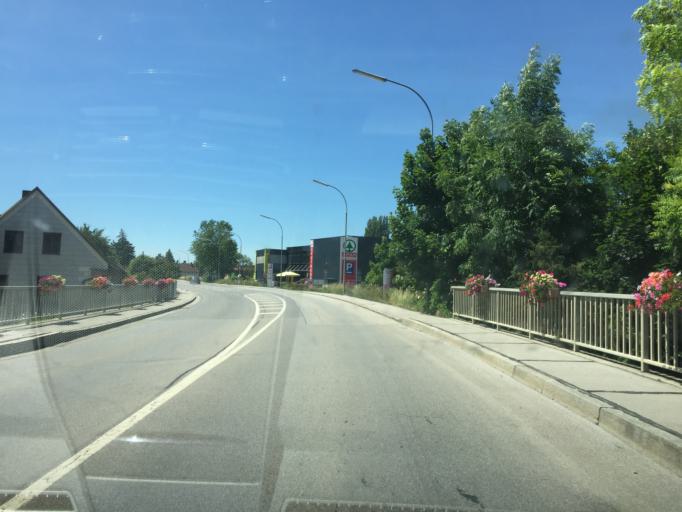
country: AT
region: Lower Austria
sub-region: Politischer Bezirk Sankt Polten
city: Herzogenburg
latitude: 48.2379
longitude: 15.6954
